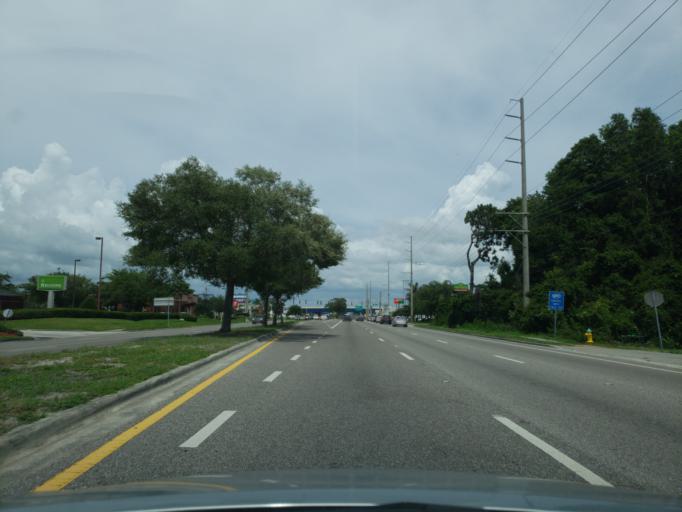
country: US
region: Florida
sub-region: Hillsborough County
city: Town 'n' Country
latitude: 28.0256
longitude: -82.5488
